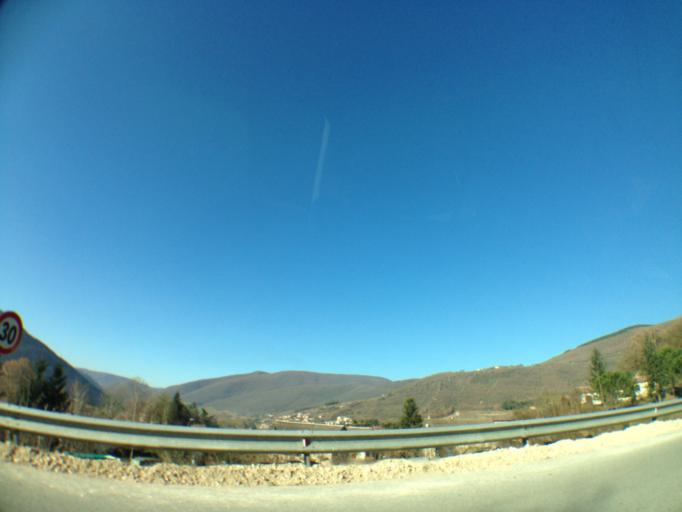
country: IT
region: Umbria
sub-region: Provincia di Perugia
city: Norcia
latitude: 42.7975
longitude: 13.0991
